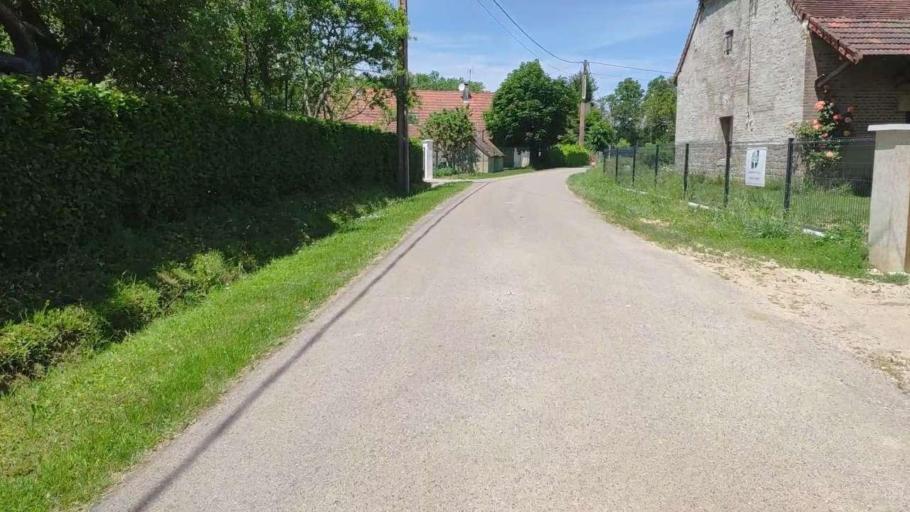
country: FR
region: Franche-Comte
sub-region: Departement du Jura
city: Bletterans
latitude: 46.8017
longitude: 5.3876
